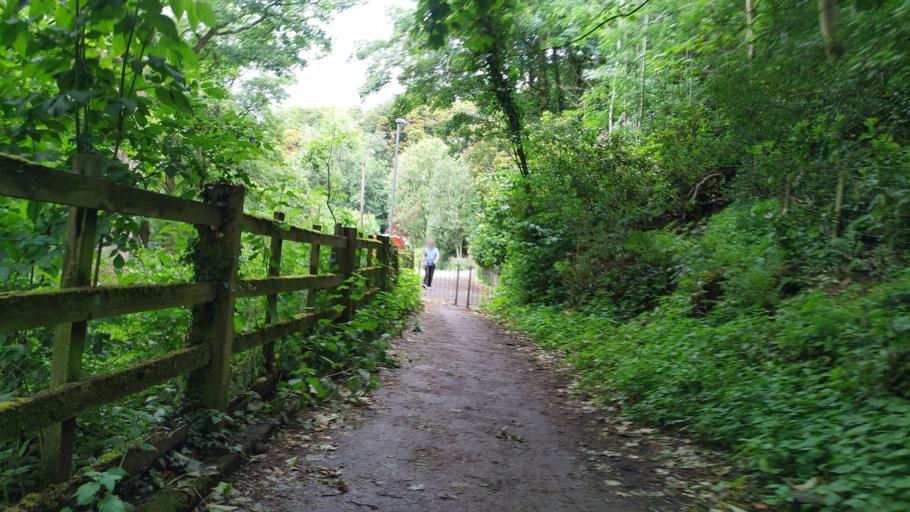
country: GB
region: England
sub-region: Lancashire
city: Chorley
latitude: 53.6879
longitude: -2.6057
